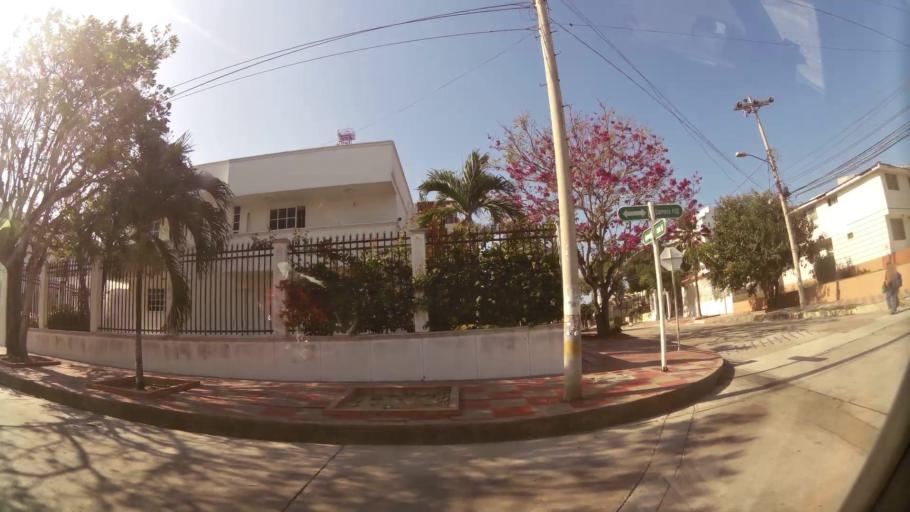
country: CO
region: Atlantico
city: Barranquilla
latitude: 11.0001
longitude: -74.8285
